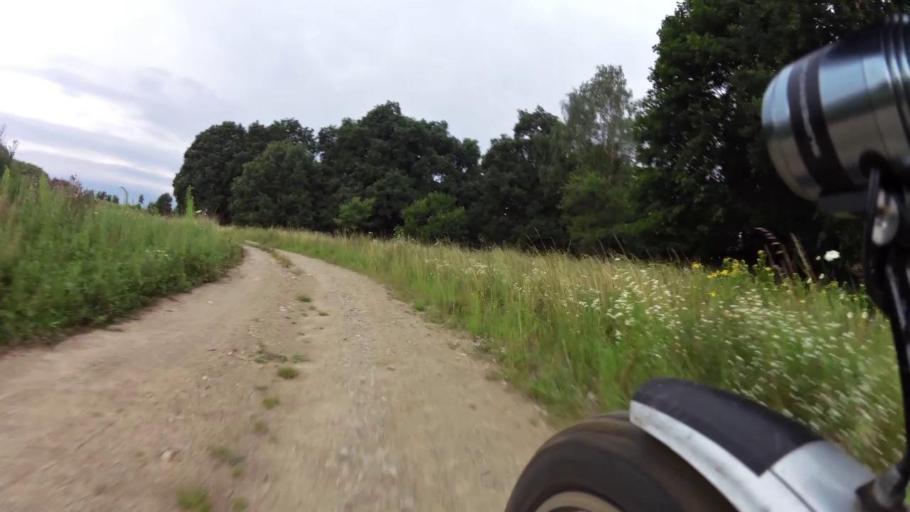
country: PL
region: West Pomeranian Voivodeship
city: Trzcinsko Zdroj
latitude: 52.8770
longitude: 14.5943
